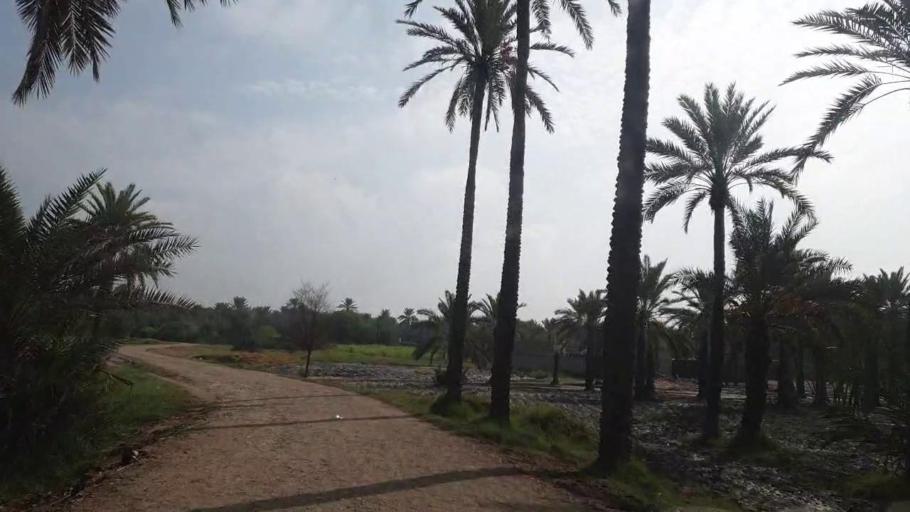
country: PK
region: Sindh
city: Khairpur
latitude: 27.5805
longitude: 68.7685
